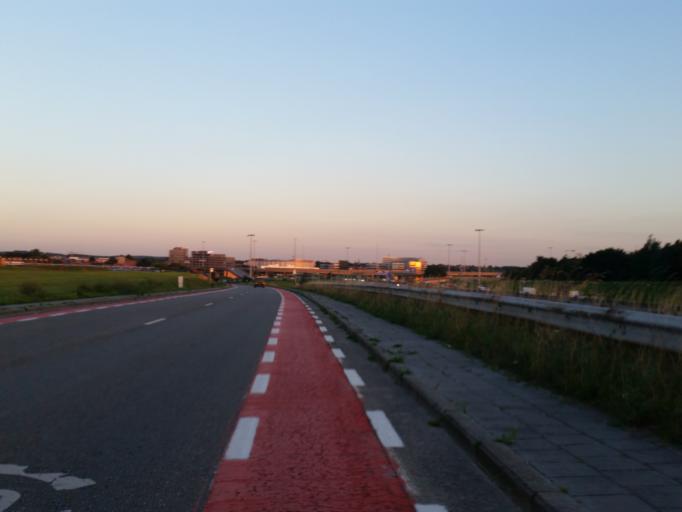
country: BE
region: Flanders
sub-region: Provincie Vlaams-Brabant
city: Diegem
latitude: 50.8976
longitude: 4.4449
